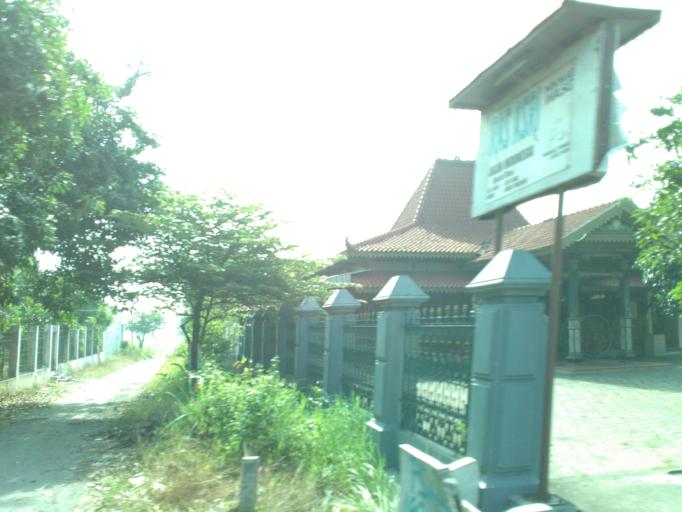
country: ID
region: Central Java
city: Delanggu
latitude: -7.6367
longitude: 110.6919
